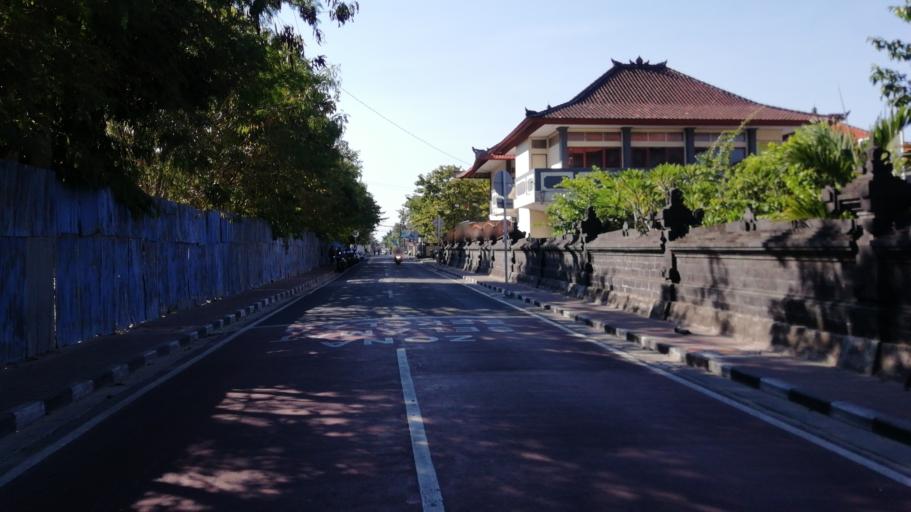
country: ID
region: Bali
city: Bualu
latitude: -8.7615
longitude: 115.2220
